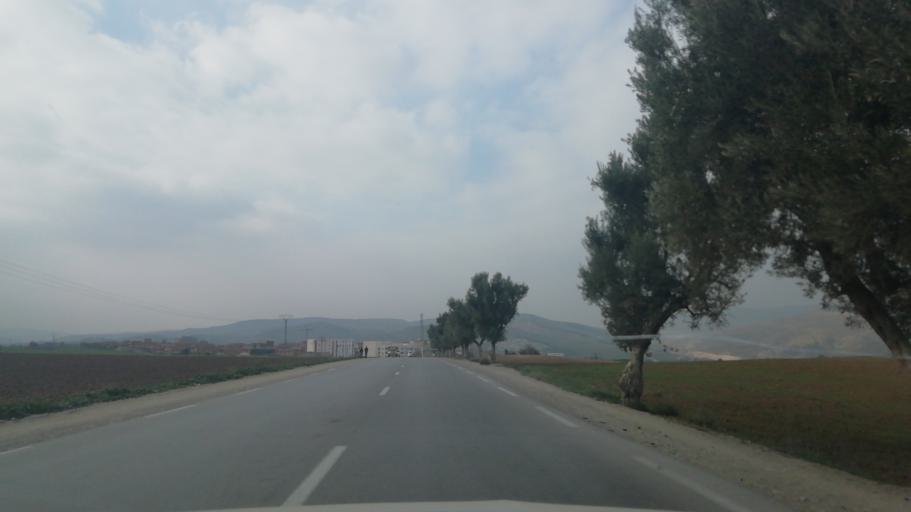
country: DZ
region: Mascara
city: Mascara
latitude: 35.4541
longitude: 0.0091
